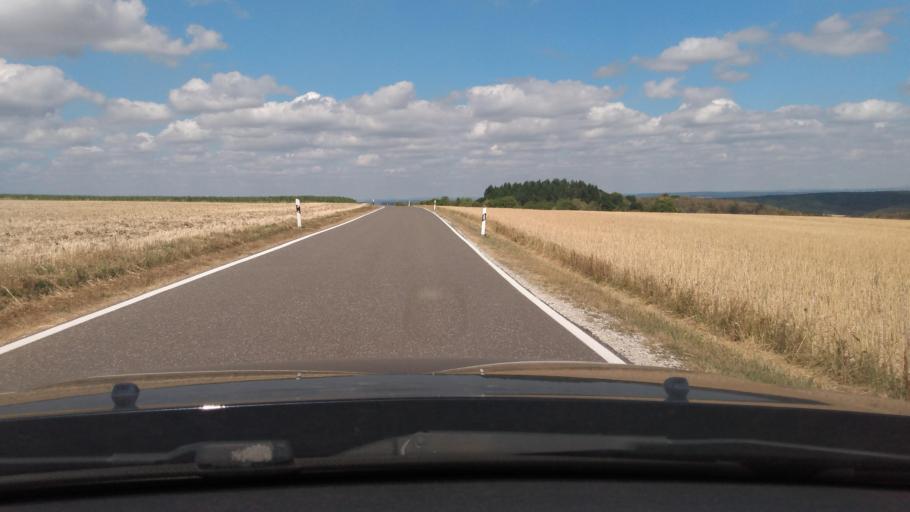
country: DE
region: Rheinland-Pfalz
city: Kleinich
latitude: 49.8884
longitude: 7.1625
